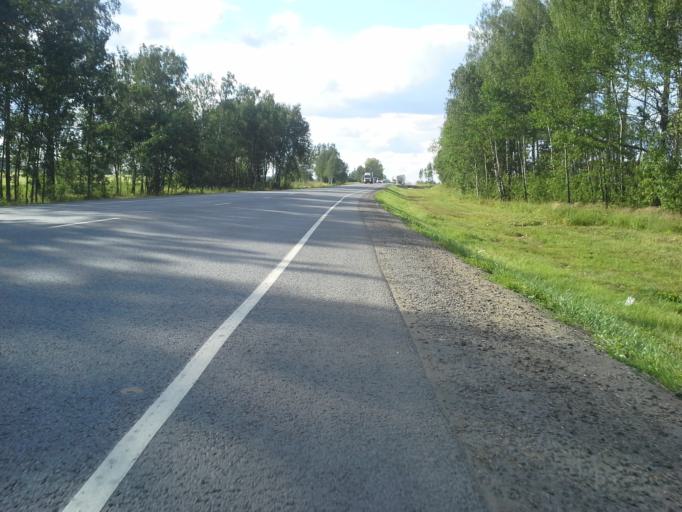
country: RU
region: Moskovskaya
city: Klimovsk
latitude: 55.3532
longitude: 37.4431
